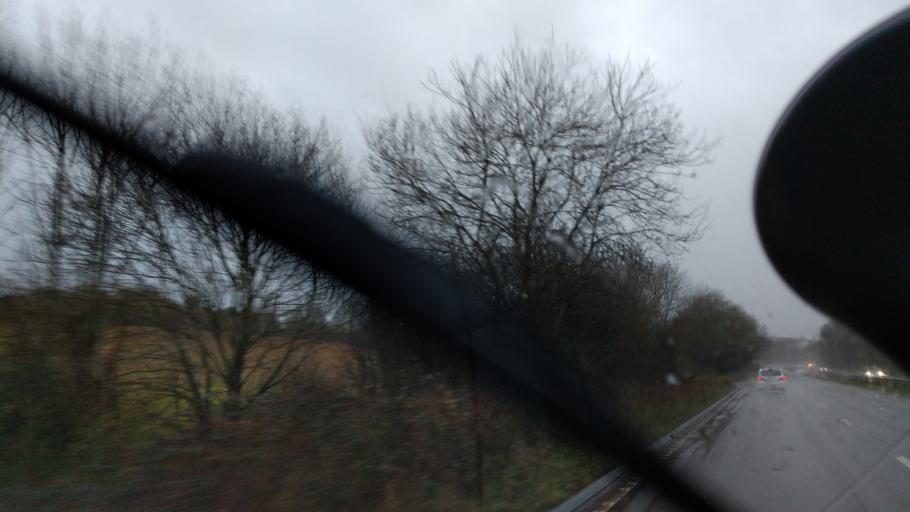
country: GB
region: England
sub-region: East Sussex
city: Lewes
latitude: 50.8658
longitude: -0.0355
